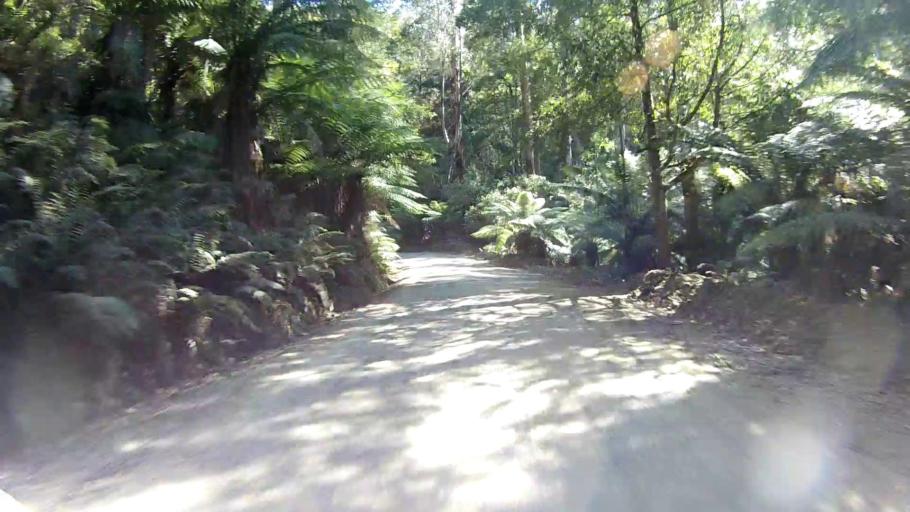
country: AU
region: Tasmania
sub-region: Derwent Valley
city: New Norfolk
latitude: -42.6797
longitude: 146.6972
